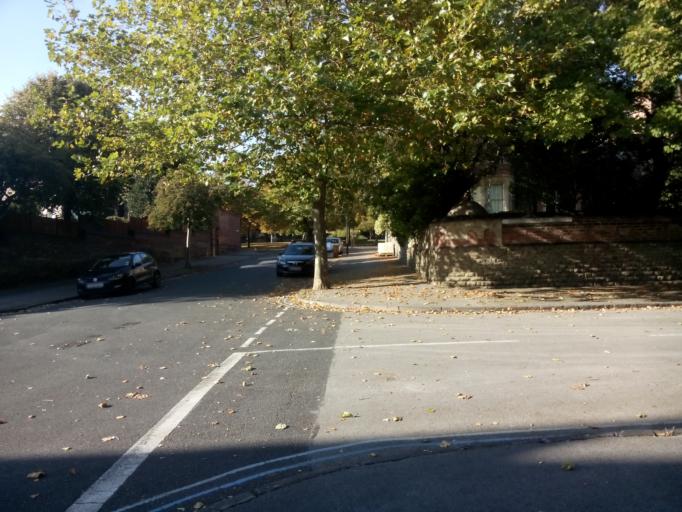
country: GB
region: England
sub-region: Nottingham
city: Nottingham
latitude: 52.9497
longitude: -1.1631
